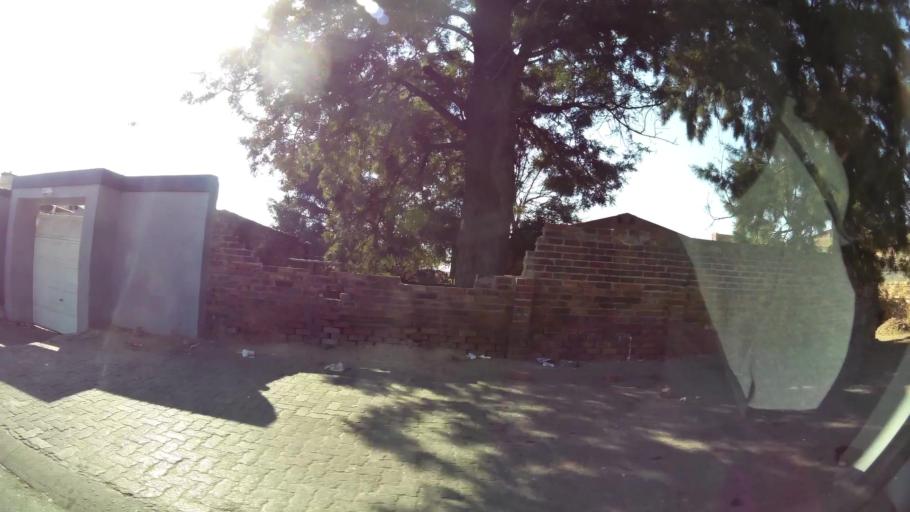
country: ZA
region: Gauteng
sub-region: City of Johannesburg Metropolitan Municipality
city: Modderfontein
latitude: -26.1100
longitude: 28.0918
